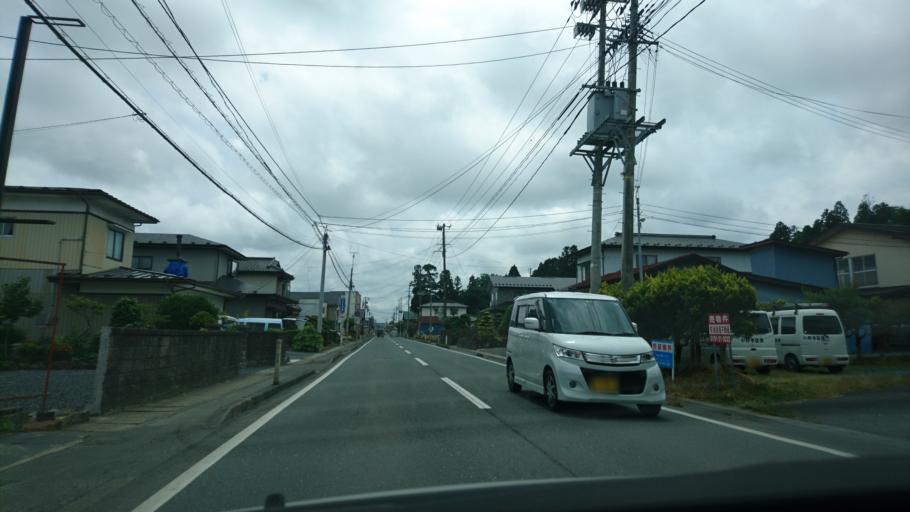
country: JP
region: Iwate
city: Ichinoseki
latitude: 38.9558
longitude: 141.1296
